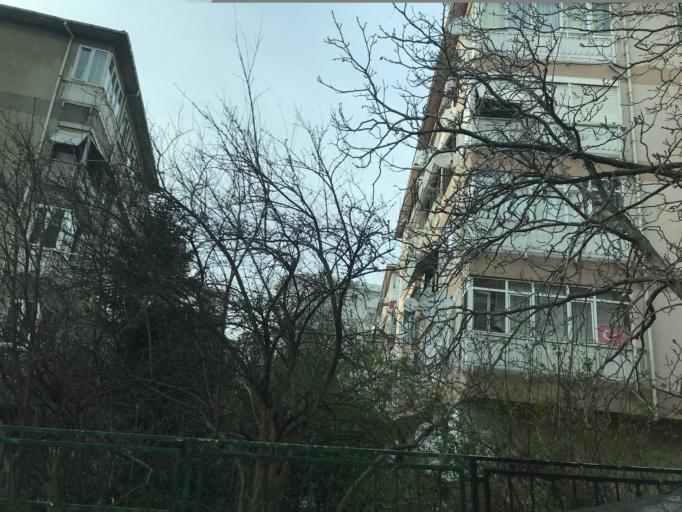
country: TR
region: Istanbul
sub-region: Atasehir
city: Atasehir
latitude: 40.9622
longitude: 29.0931
